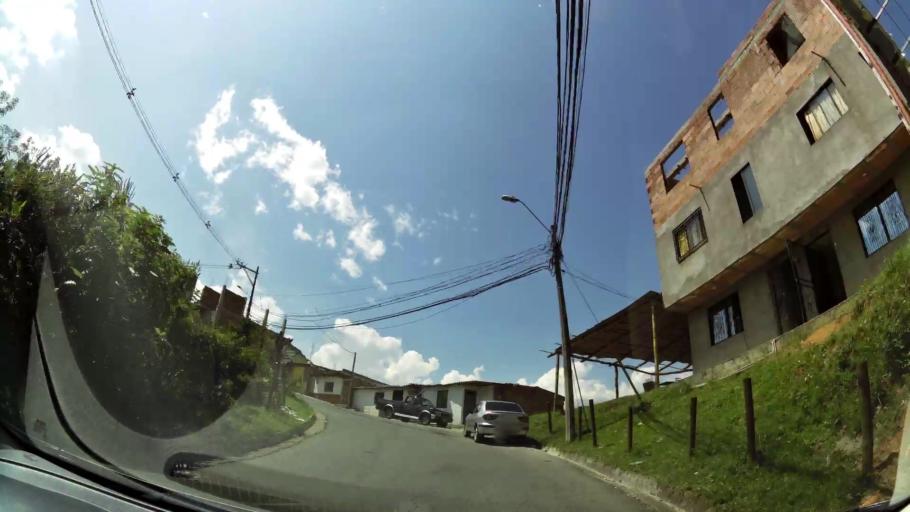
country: CO
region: Antioquia
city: Itagui
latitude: 6.2082
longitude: -75.6080
